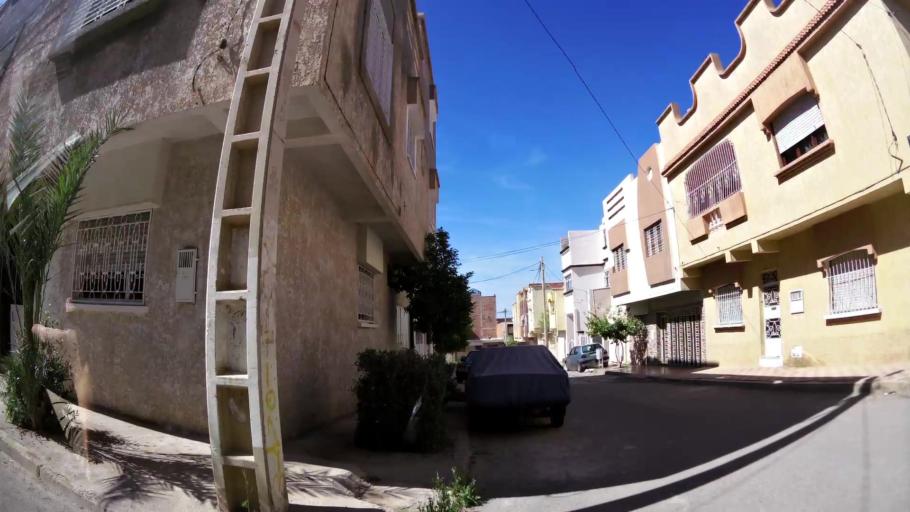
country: MA
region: Oriental
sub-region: Oujda-Angad
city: Oujda
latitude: 34.6556
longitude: -1.9163
